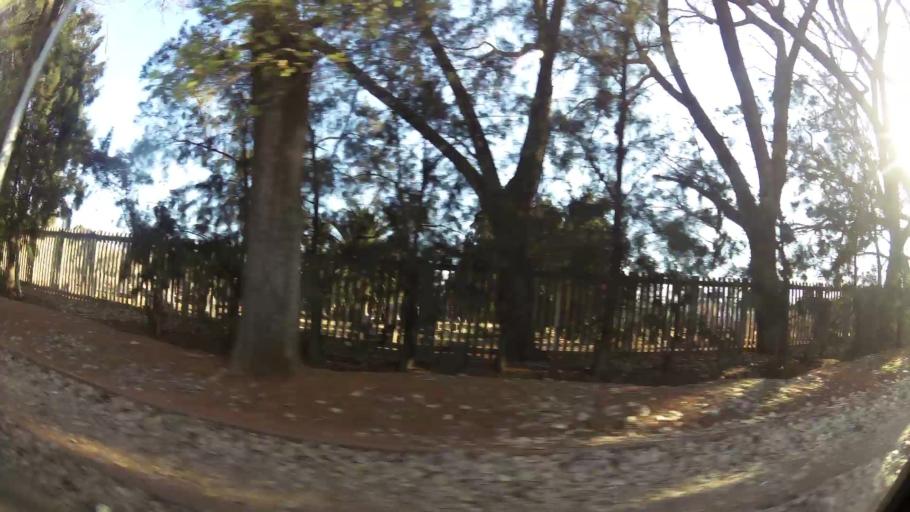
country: ZA
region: Gauteng
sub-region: Ekurhuleni Metropolitan Municipality
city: Germiston
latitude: -26.1973
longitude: 28.1461
